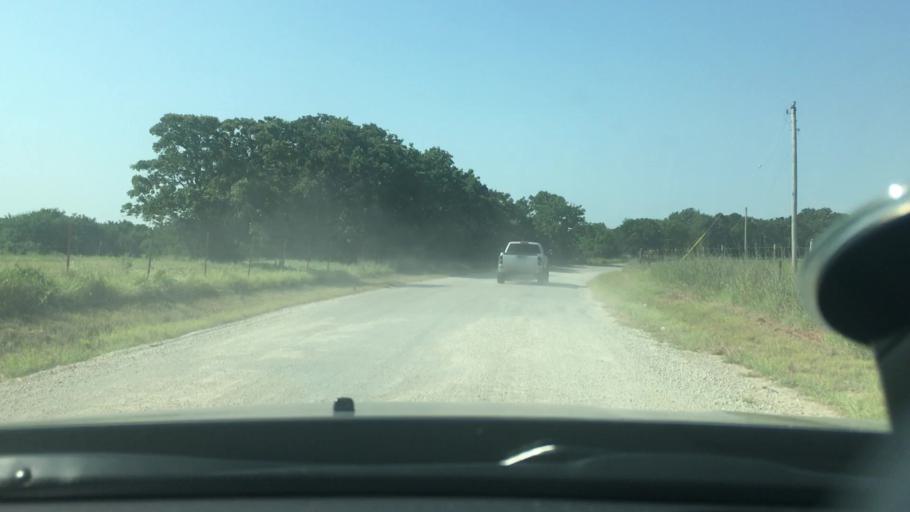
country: US
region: Oklahoma
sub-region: Garvin County
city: Lindsay
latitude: 34.7705
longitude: -97.6122
